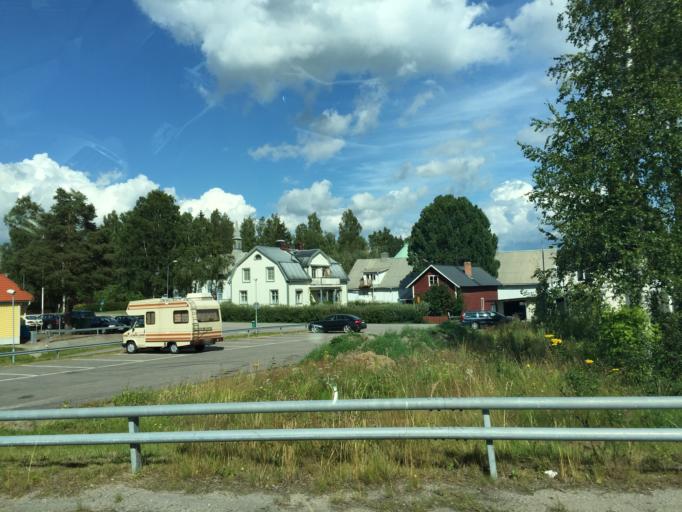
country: SE
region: Gaevleborg
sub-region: Bollnas Kommun
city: Kilafors
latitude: 61.2293
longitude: 16.5644
